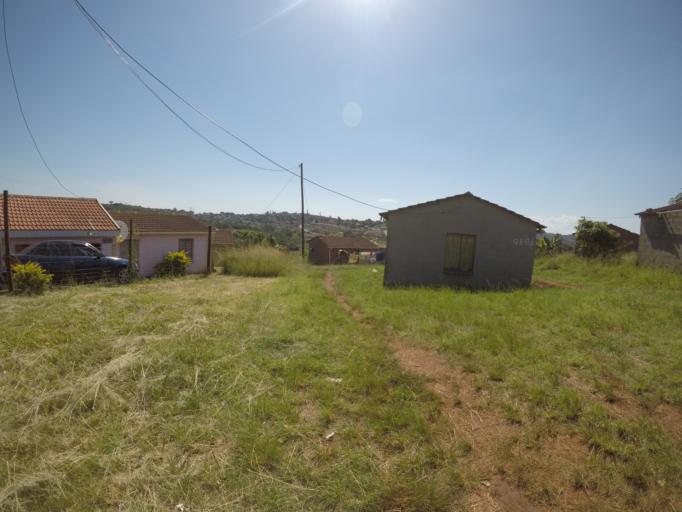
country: ZA
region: KwaZulu-Natal
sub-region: uThungulu District Municipality
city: Empangeni
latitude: -28.7727
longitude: 31.8762
